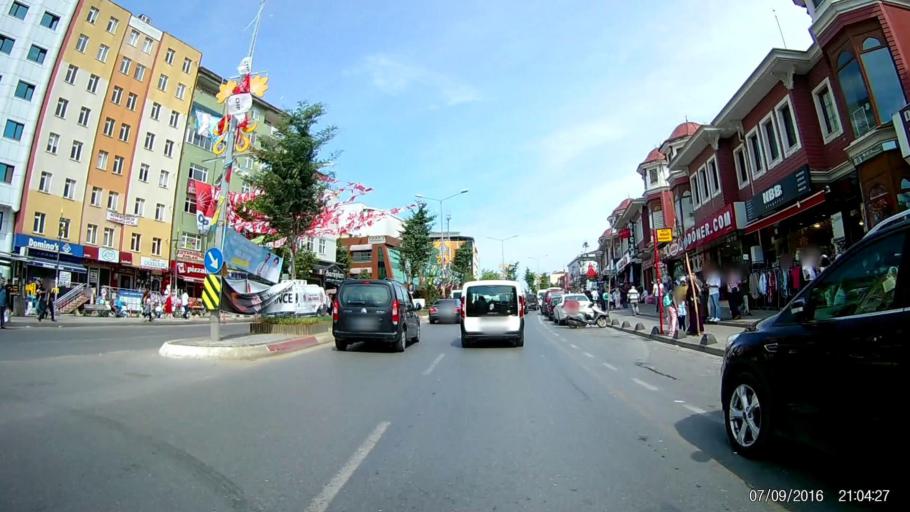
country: TR
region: Istanbul
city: Sultanbeyli
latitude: 40.9692
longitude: 29.2577
